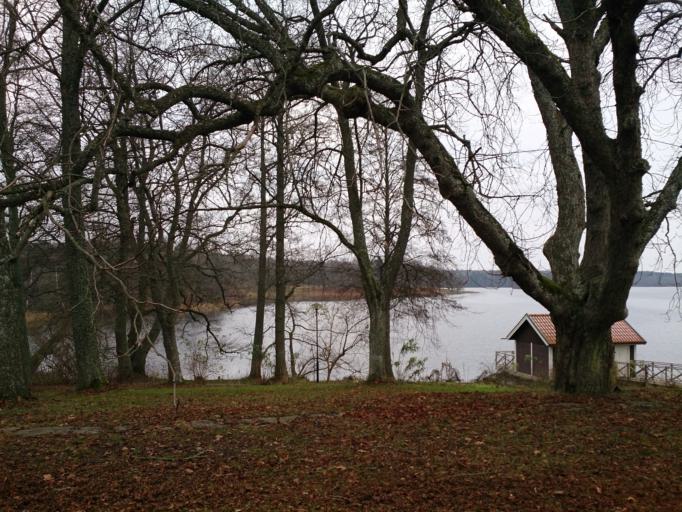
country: SE
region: OEstergoetland
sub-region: Atvidabergs Kommun
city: Atvidaberg
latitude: 58.1921
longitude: 15.9952
